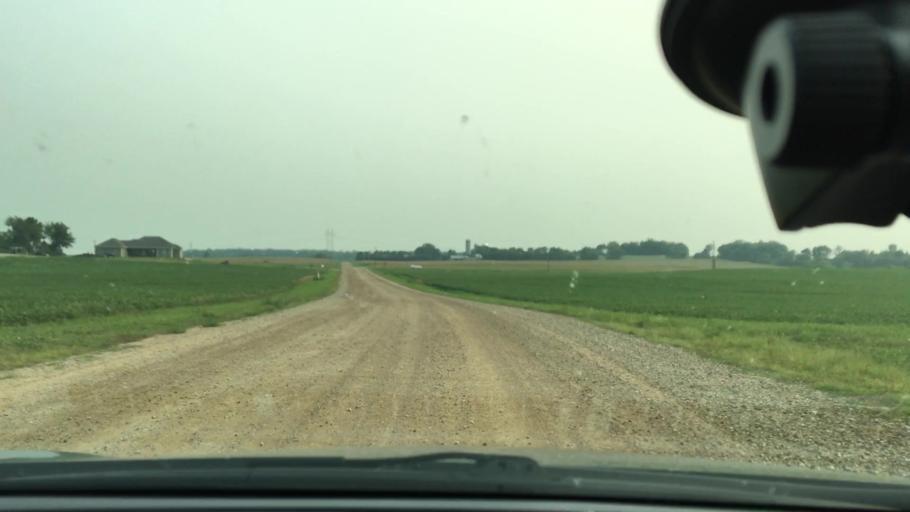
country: US
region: Minnesota
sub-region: Wright County
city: Albertville
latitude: 45.2416
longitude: -93.6286
